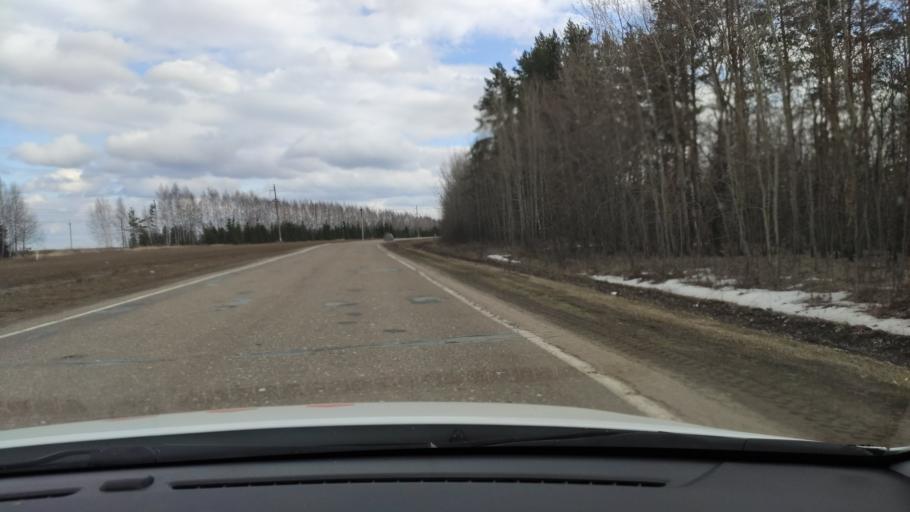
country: RU
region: Tatarstan
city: Vysokaya Gora
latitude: 56.0631
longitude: 49.2032
